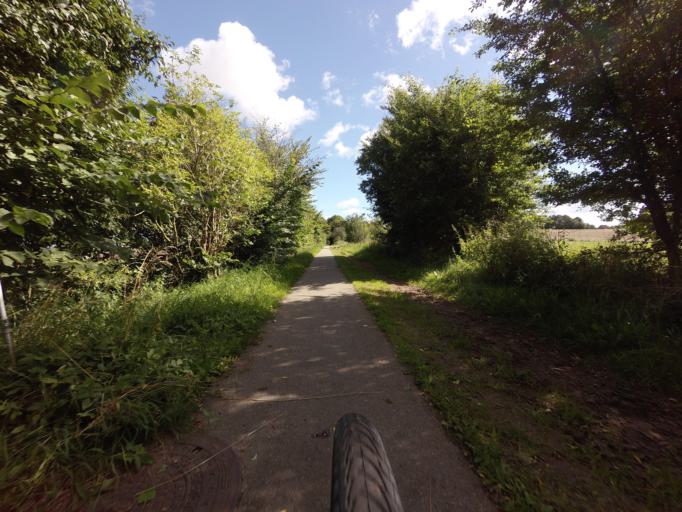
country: DK
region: Central Jutland
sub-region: Horsens Kommune
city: Braedstrup
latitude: 55.9691
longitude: 9.7115
